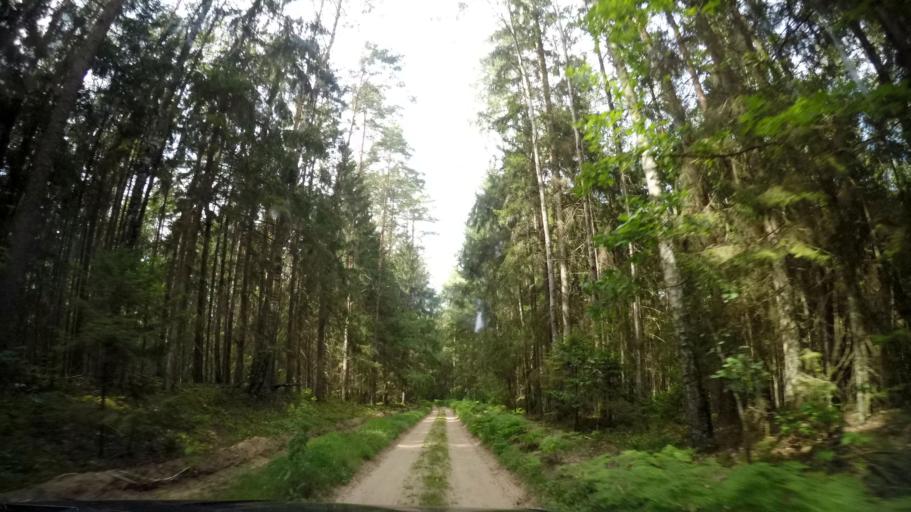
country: BY
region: Grodnenskaya
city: Skidal'
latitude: 53.8279
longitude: 24.1792
